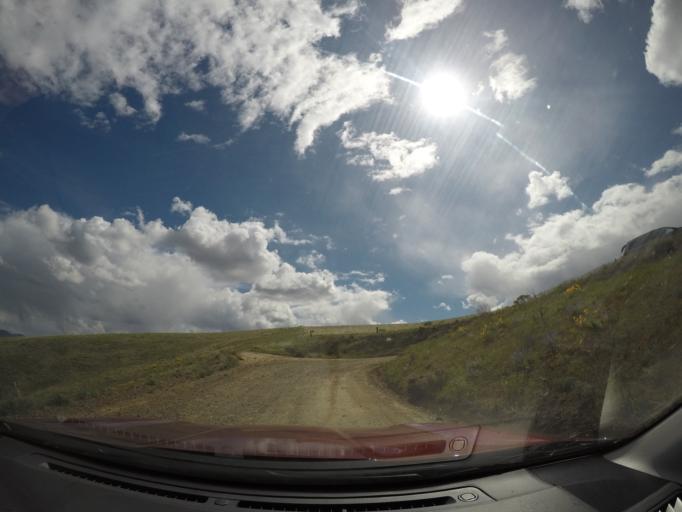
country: US
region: Washington
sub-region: Chelan County
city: West Wenatchee
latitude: 47.4621
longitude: -120.3819
